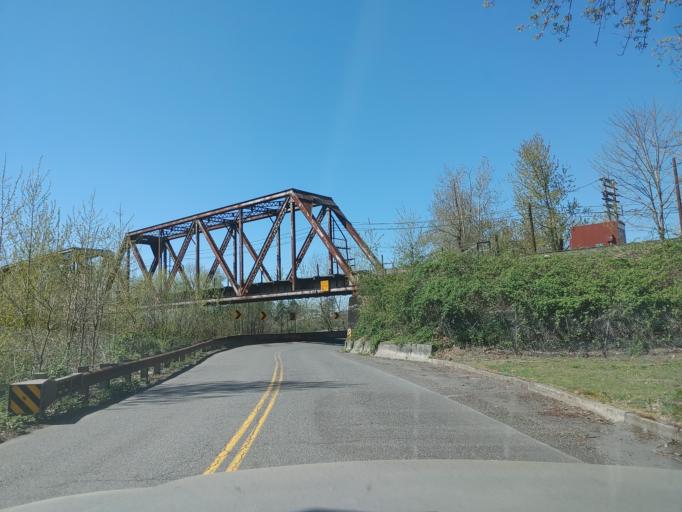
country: US
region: Oregon
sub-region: Multnomah County
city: Troutdale
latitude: 45.5417
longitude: -122.3809
